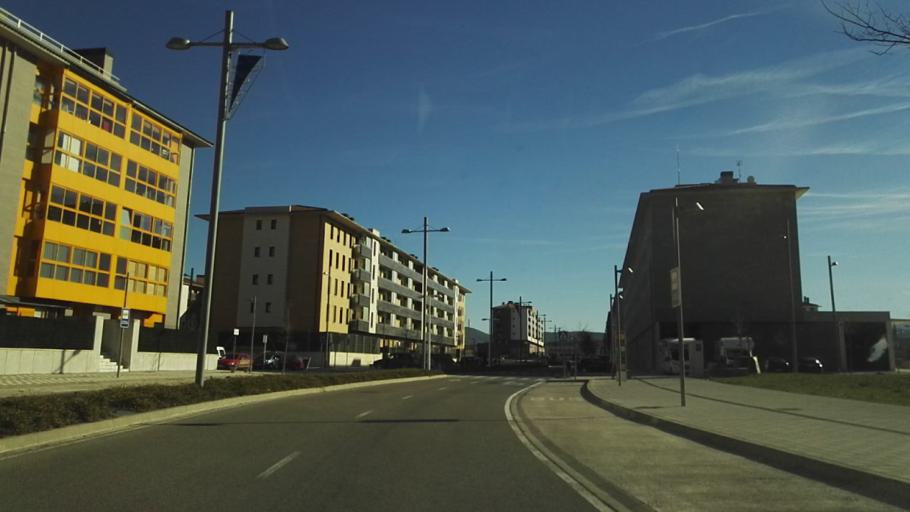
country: ES
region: Navarre
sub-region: Provincia de Navarra
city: Burlata
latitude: 42.7956
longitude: -1.6177
